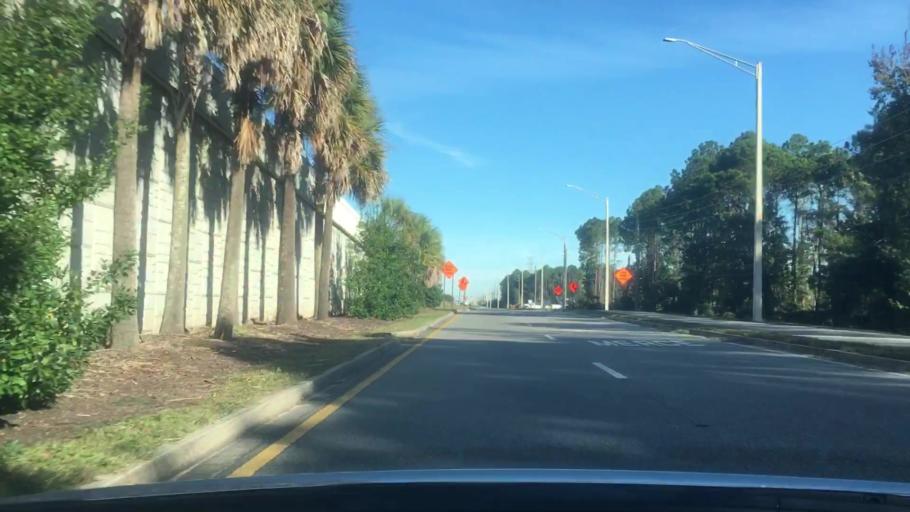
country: US
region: Florida
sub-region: Duval County
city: Neptune Beach
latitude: 30.2885
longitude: -81.4887
